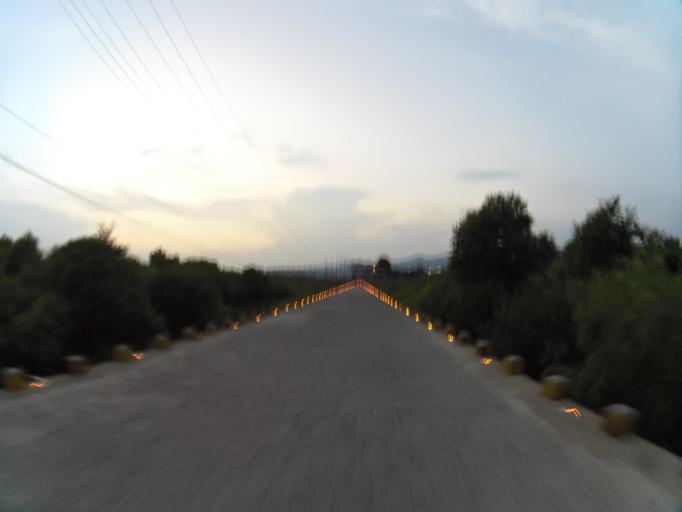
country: KR
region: Gyeongsangbuk-do
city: Gyeongsan-si
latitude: 35.8568
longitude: 128.7398
